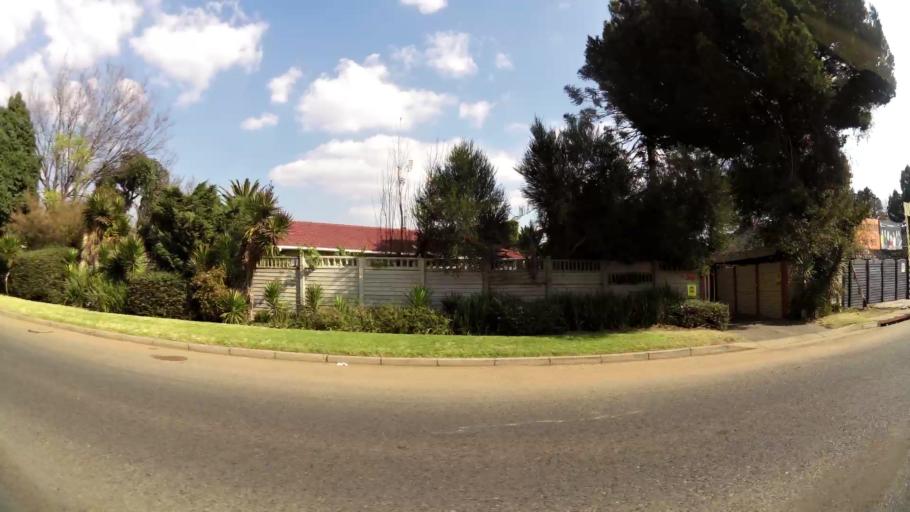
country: ZA
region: Gauteng
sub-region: City of Johannesburg Metropolitan Municipality
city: Modderfontein
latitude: -26.0963
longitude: 28.2510
